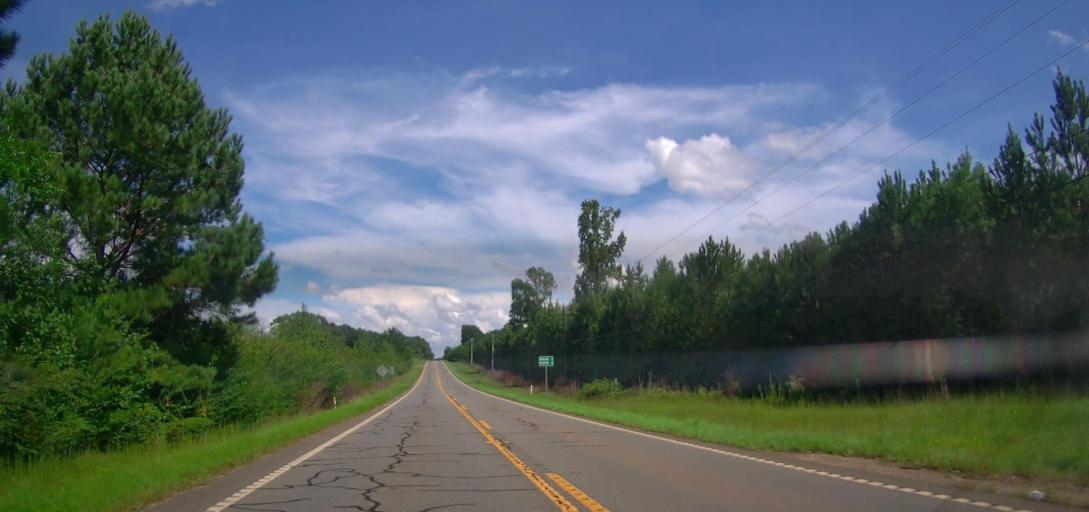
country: US
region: Georgia
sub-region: Talbot County
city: Sardis
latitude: 32.8002
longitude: -84.5862
